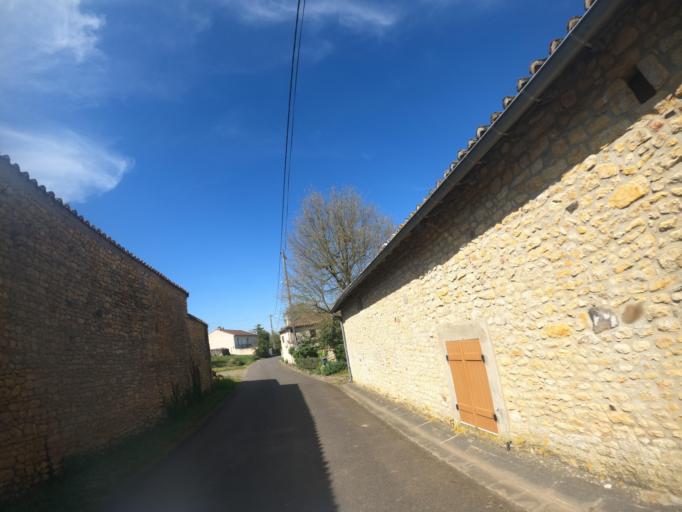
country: FR
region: Poitou-Charentes
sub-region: Departement des Deux-Sevres
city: Saint-Varent
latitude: 46.9095
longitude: -0.2141
